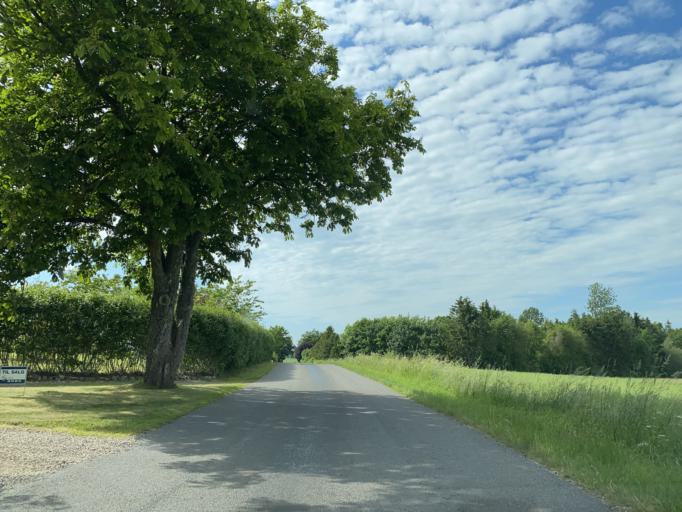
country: DK
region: Central Jutland
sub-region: Skanderborg Kommune
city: Galten
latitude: 56.2071
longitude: 9.9067
